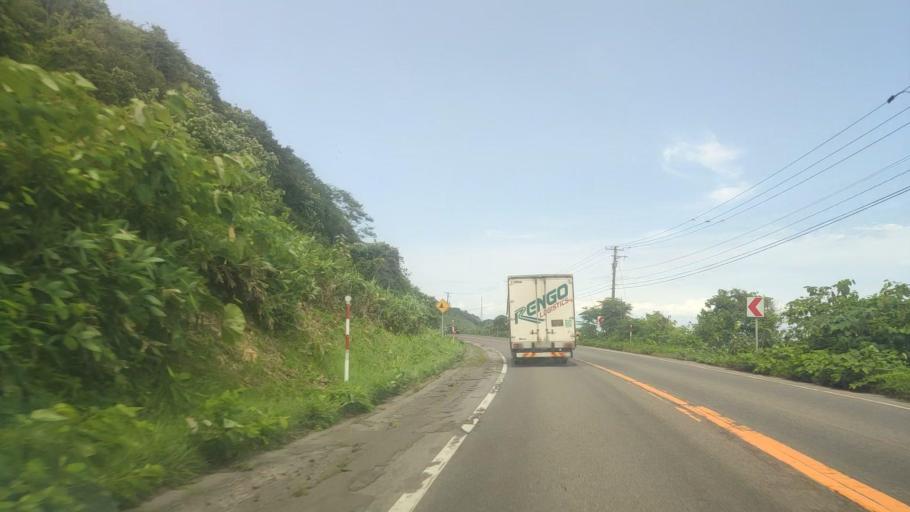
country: JP
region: Hokkaido
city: Nanae
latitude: 42.1626
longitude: 140.4693
